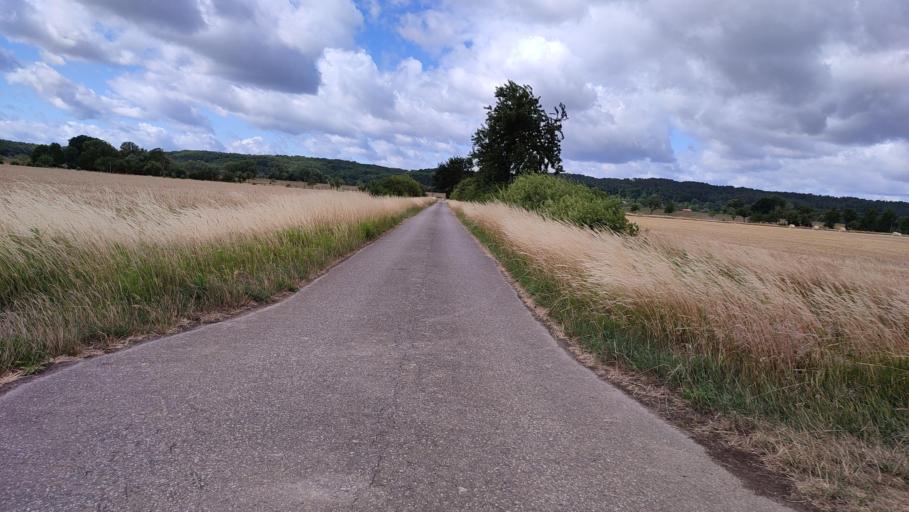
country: DE
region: Lower Saxony
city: Neu Darchau
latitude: 53.2221
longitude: 10.9476
